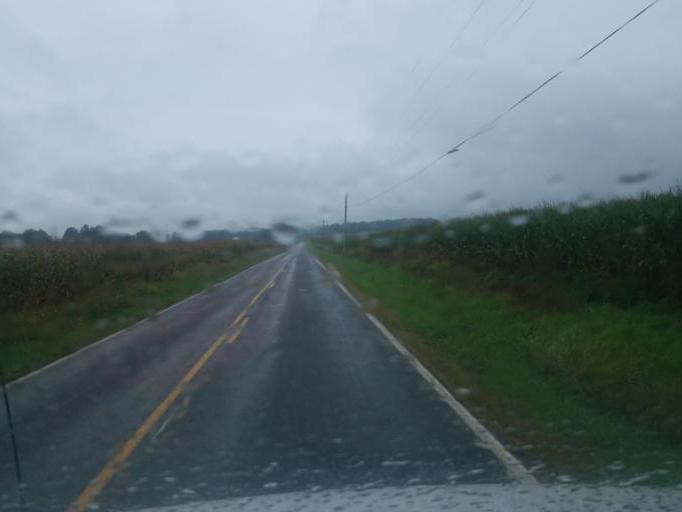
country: US
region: Ohio
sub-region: Wayne County
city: Rittman
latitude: 41.0062
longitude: -81.8152
